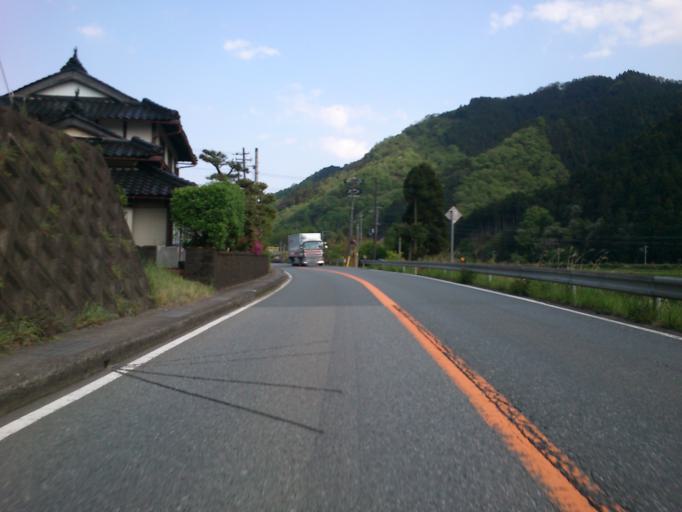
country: JP
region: Kyoto
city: Fukuchiyama
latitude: 35.3248
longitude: 134.9680
